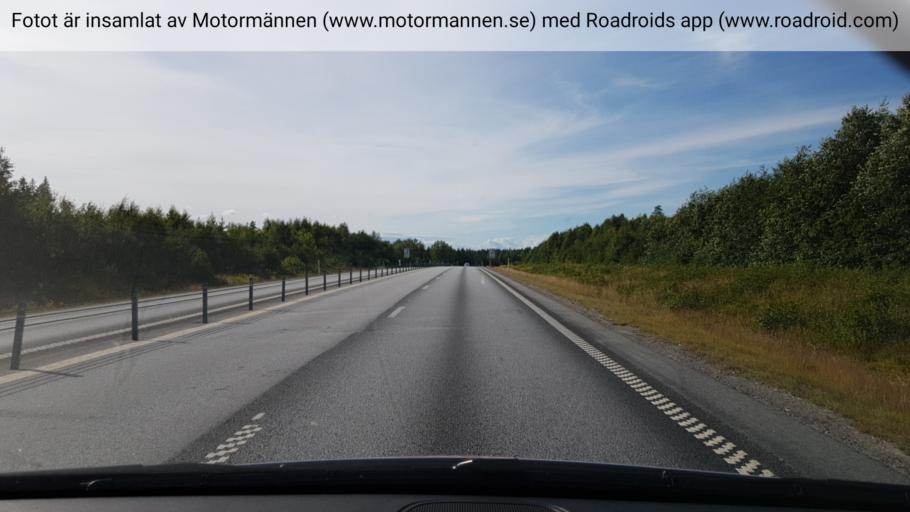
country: SE
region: Vaesterbotten
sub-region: Vannas Kommun
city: Vannasby
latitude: 63.8987
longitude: 19.9095
